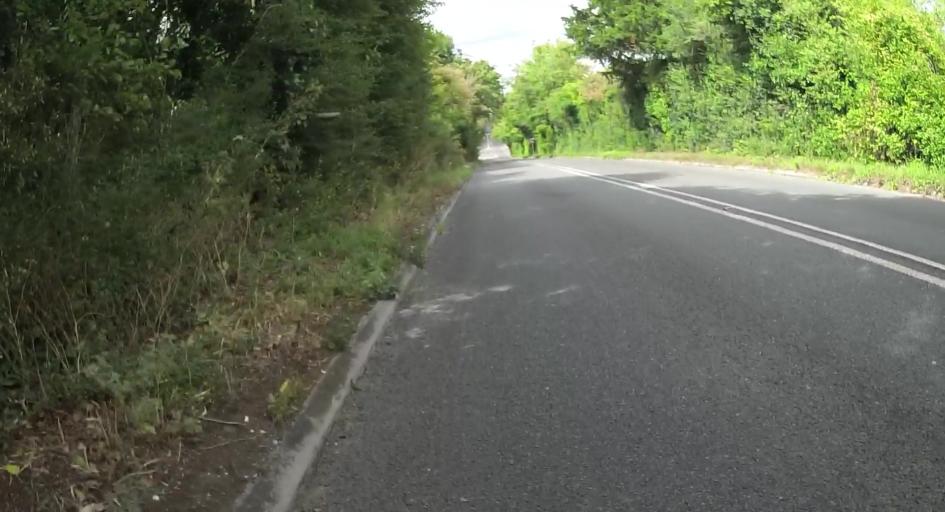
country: GB
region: England
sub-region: Hampshire
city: Kings Worthy
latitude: 51.1092
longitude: -1.3438
